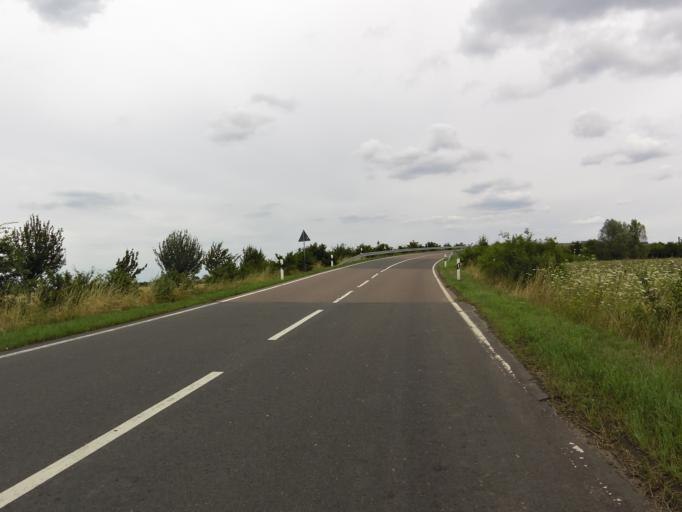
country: DE
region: Saxony
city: Rackwitz
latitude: 51.4159
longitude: 12.3788
